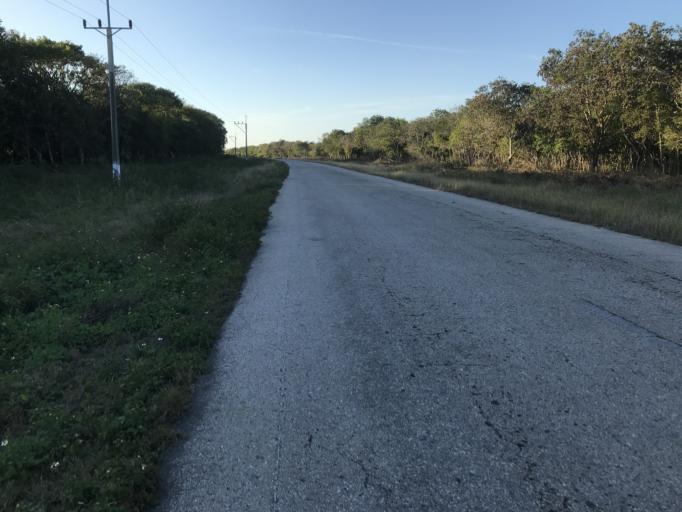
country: CU
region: Cienfuegos
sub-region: Municipio de Aguada de Pasajeros
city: Aguada de Pasajeros
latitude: 22.0752
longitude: -81.0603
